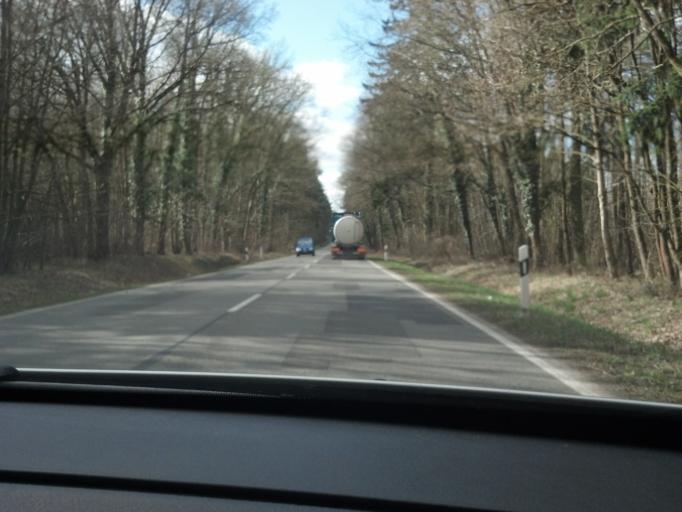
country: DE
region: Mecklenburg-Vorpommern
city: Plau am See
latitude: 53.3794
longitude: 12.3341
